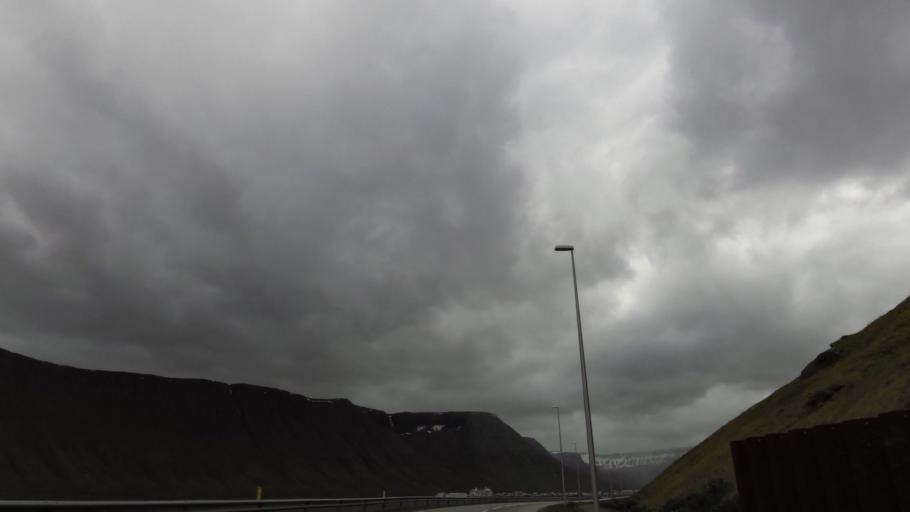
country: IS
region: Westfjords
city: Isafjoerdur
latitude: 66.0925
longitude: -23.1137
